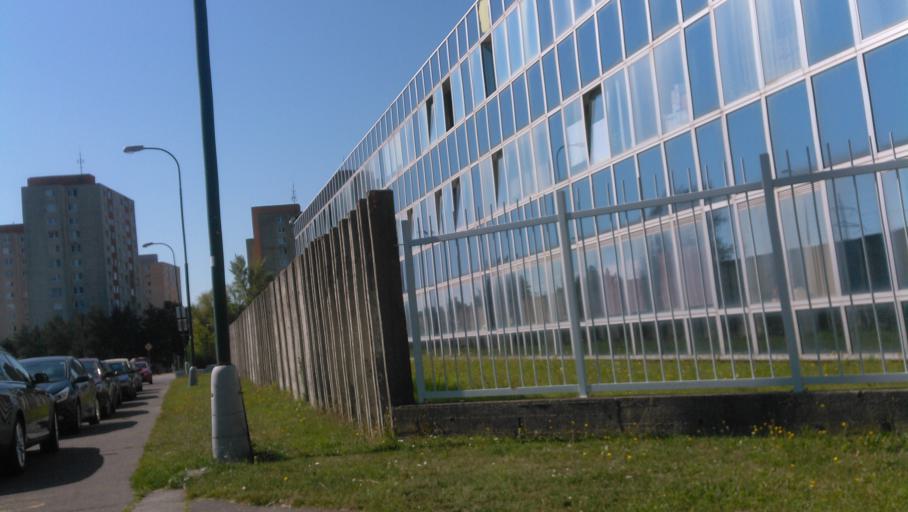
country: AT
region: Lower Austria
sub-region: Politischer Bezirk Bruck an der Leitha
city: Wolfsthal
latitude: 48.1936
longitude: 17.0403
